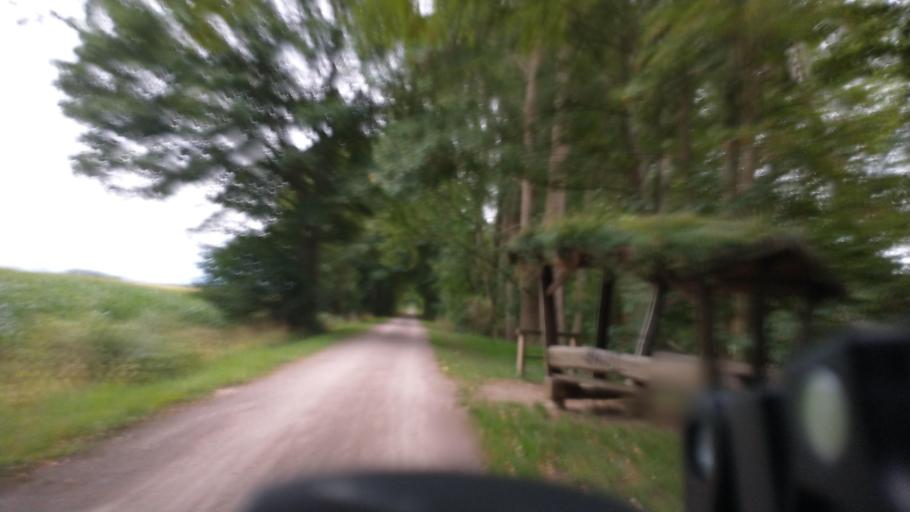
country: DE
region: Schleswig-Holstein
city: Grabau
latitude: 53.7977
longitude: 10.2973
